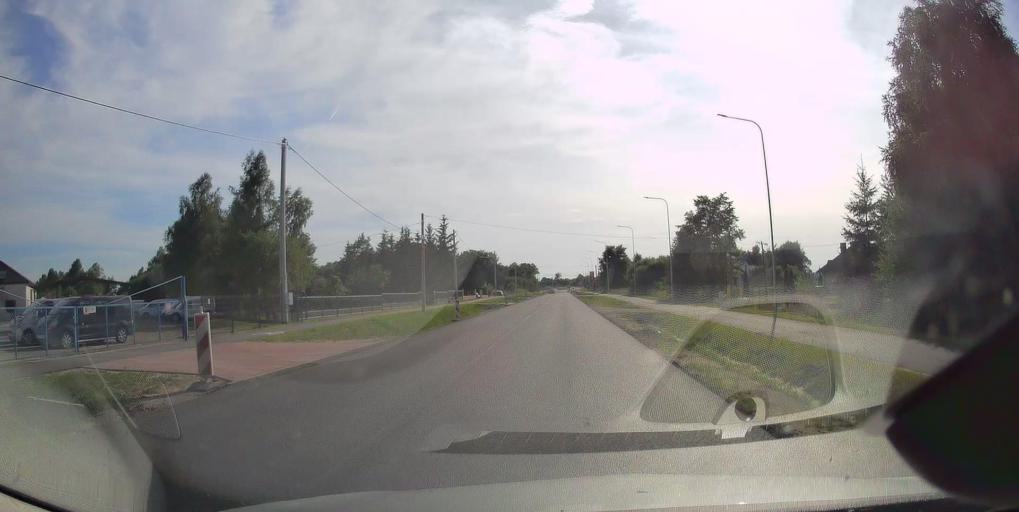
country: PL
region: Swietokrzyskie
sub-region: Powiat konecki
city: Radoszyce
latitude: 51.0737
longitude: 20.2747
